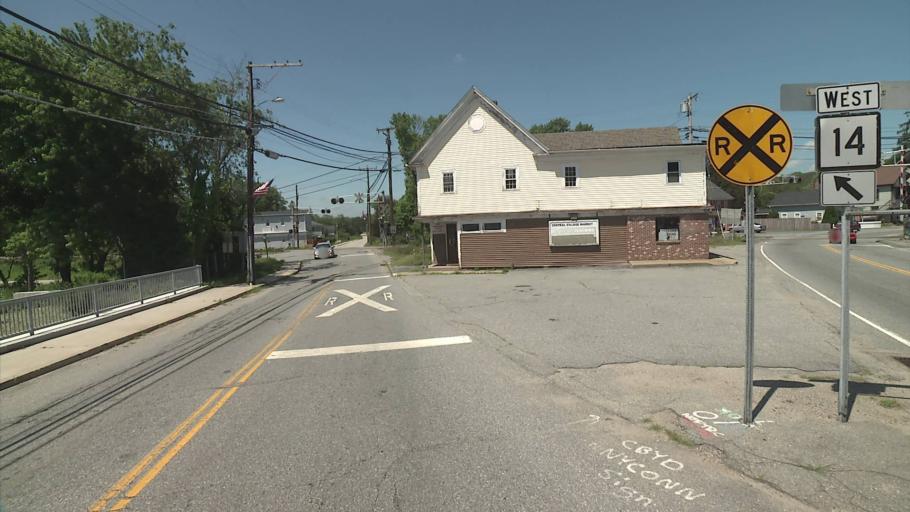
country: US
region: Connecticut
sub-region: Windham County
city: Wauregan
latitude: 41.7227
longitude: -71.9068
